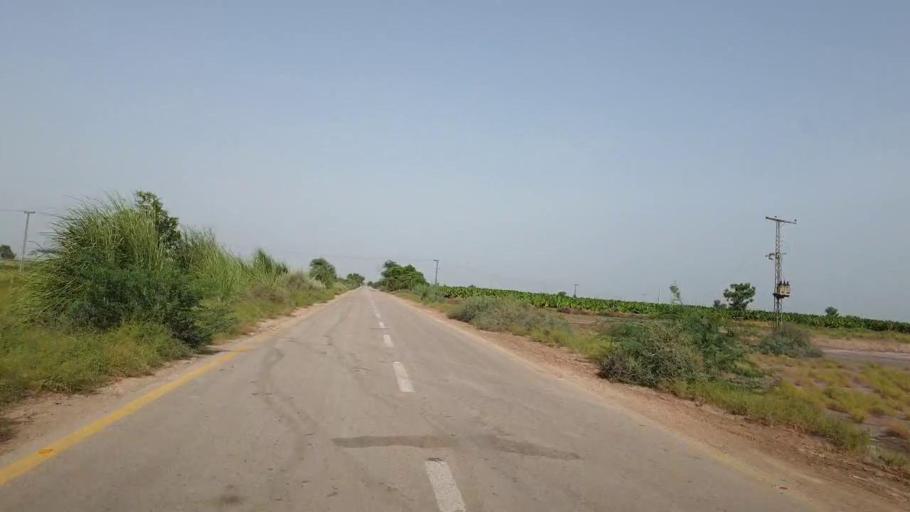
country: PK
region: Sindh
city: Bandhi
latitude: 26.5879
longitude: 68.2272
